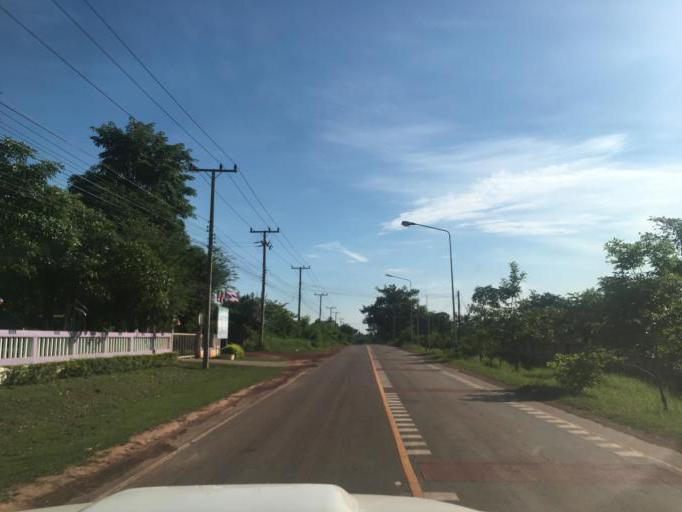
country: TH
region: Changwat Udon Thani
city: Kut Chap
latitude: 17.4765
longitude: 102.5919
